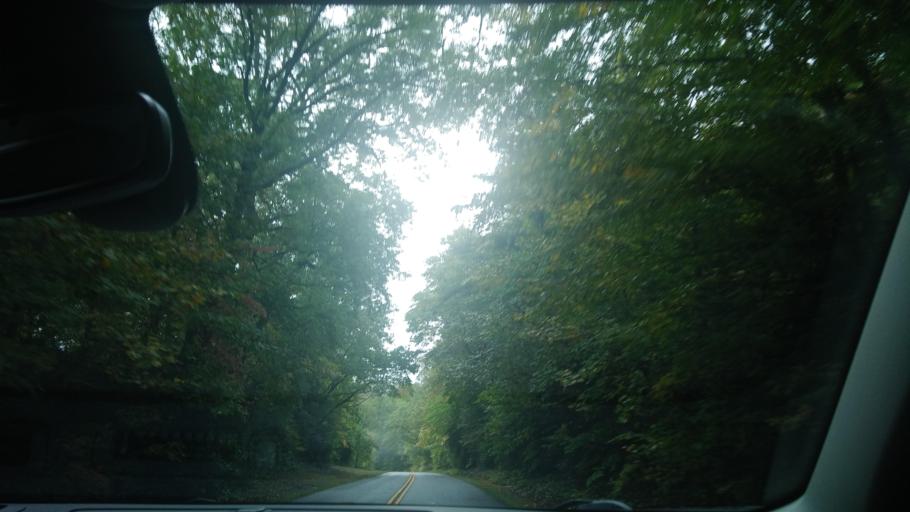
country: US
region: North Carolina
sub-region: Mitchell County
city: Spruce Pine
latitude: 35.8854
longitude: -81.9815
